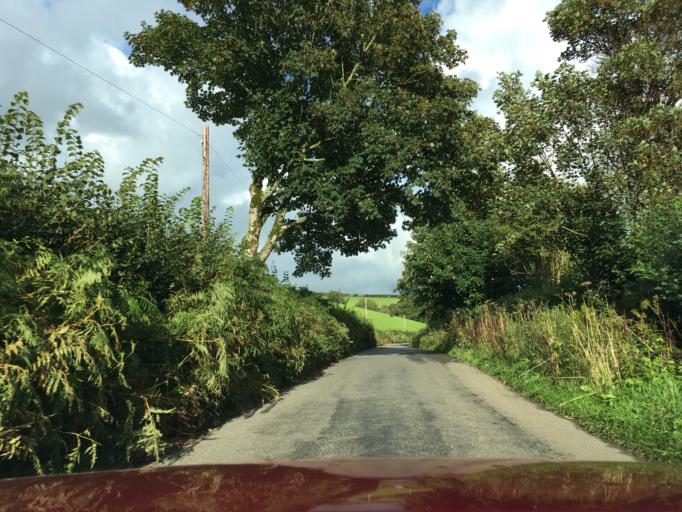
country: GB
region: England
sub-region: Devon
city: South Brent
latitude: 50.4004
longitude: -3.8008
